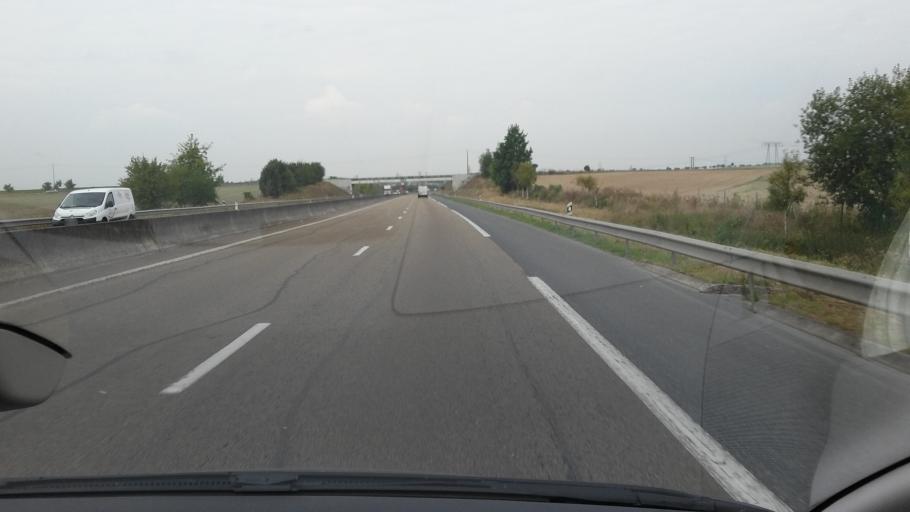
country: FR
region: Champagne-Ardenne
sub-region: Departement de la Marne
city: Cernay-les-Reims
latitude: 49.2571
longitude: 4.0855
